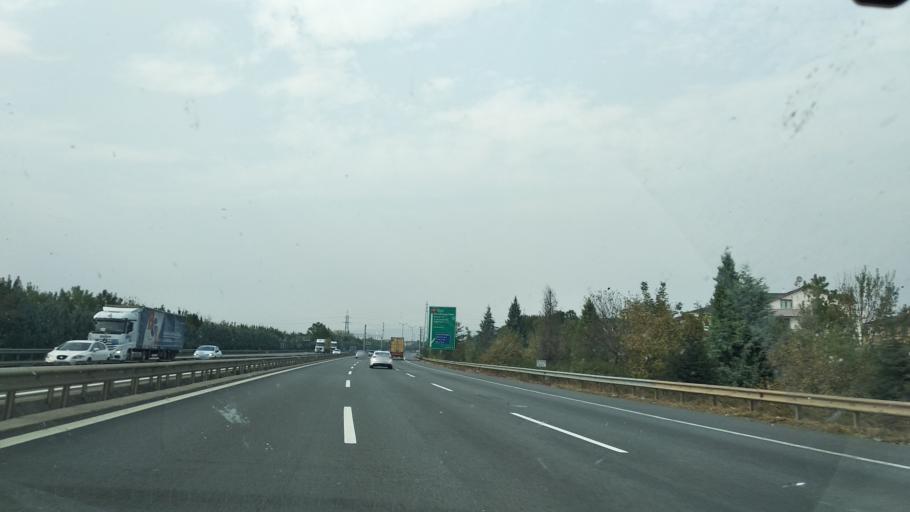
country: TR
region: Kocaeli
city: Kosekoy
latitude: 40.7394
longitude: 30.0466
